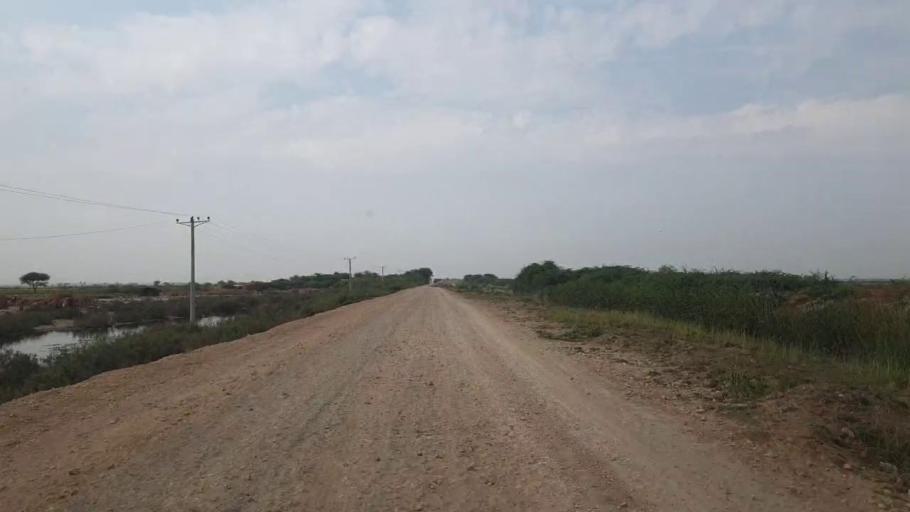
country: PK
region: Sindh
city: Kario
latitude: 24.6202
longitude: 68.5826
